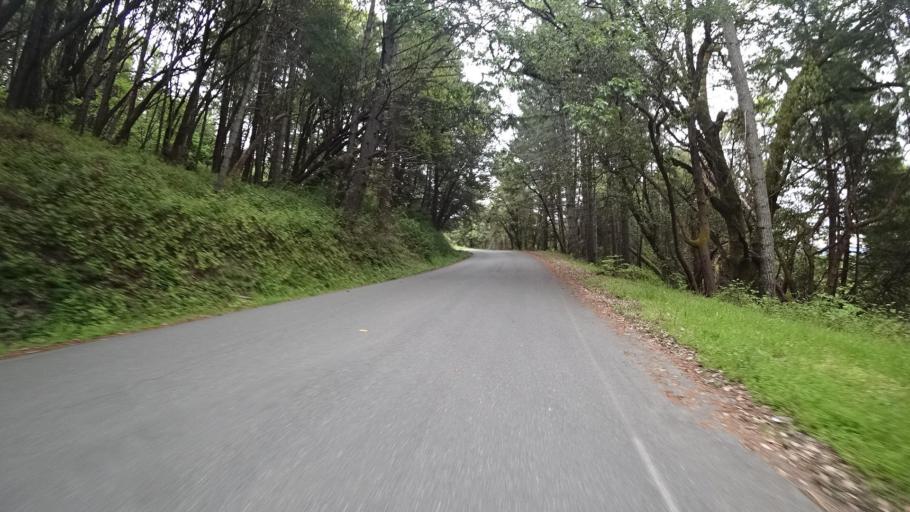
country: US
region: California
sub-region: Humboldt County
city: Willow Creek
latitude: 41.1086
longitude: -123.7131
